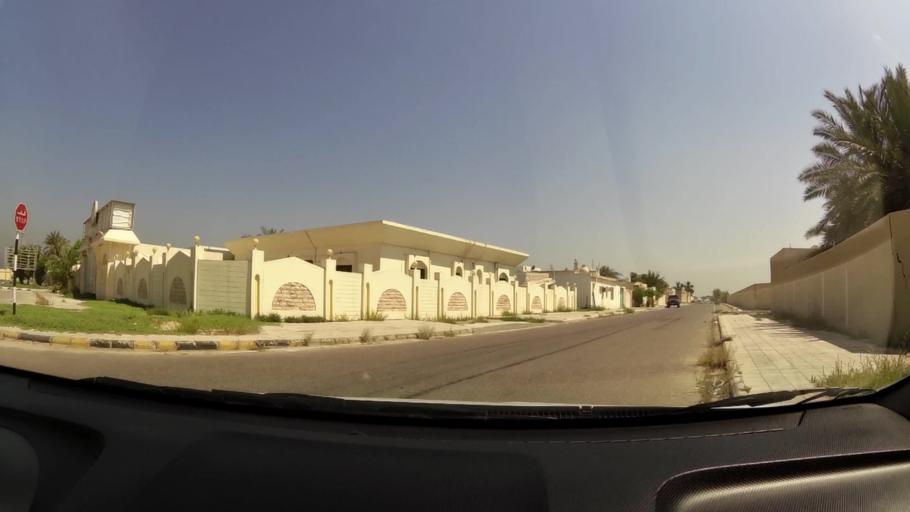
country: AE
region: Umm al Qaywayn
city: Umm al Qaywayn
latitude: 25.5585
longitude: 55.5469
